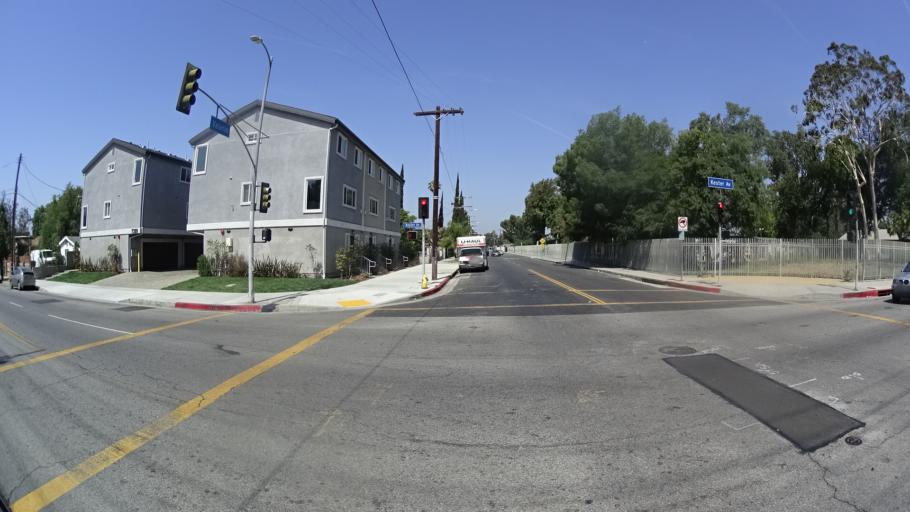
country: US
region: California
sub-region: Los Angeles County
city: Van Nuys
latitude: 34.2048
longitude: -118.4575
